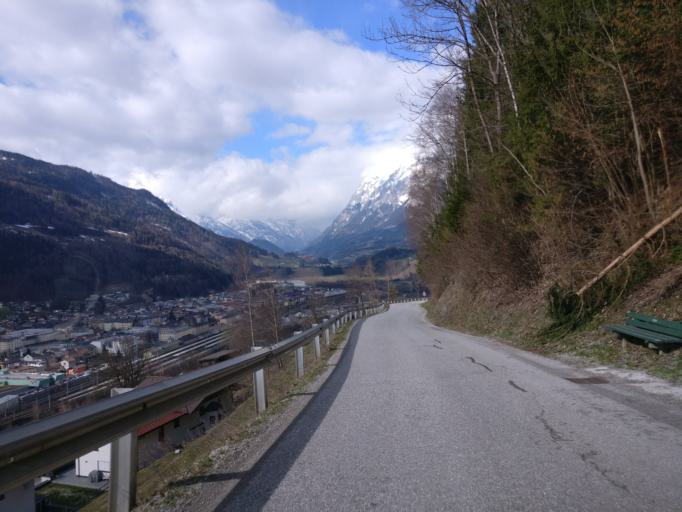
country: AT
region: Salzburg
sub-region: Politischer Bezirk Sankt Johann im Pongau
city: Bischofshofen
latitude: 47.4120
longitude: 13.2250
